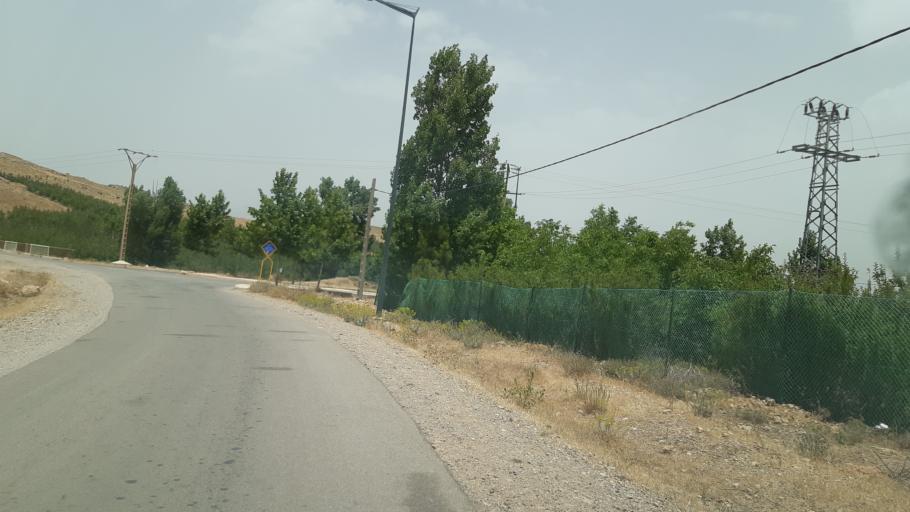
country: MA
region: Meknes-Tafilalet
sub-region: Ifrane
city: Ifrane
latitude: 33.6528
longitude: -5.0129
